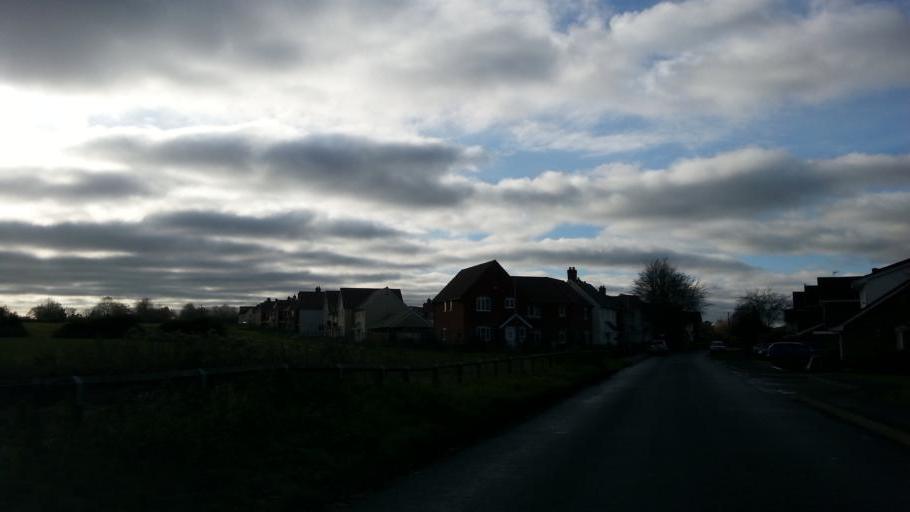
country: GB
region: England
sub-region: Suffolk
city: Ixworth
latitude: 52.3259
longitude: 0.8913
